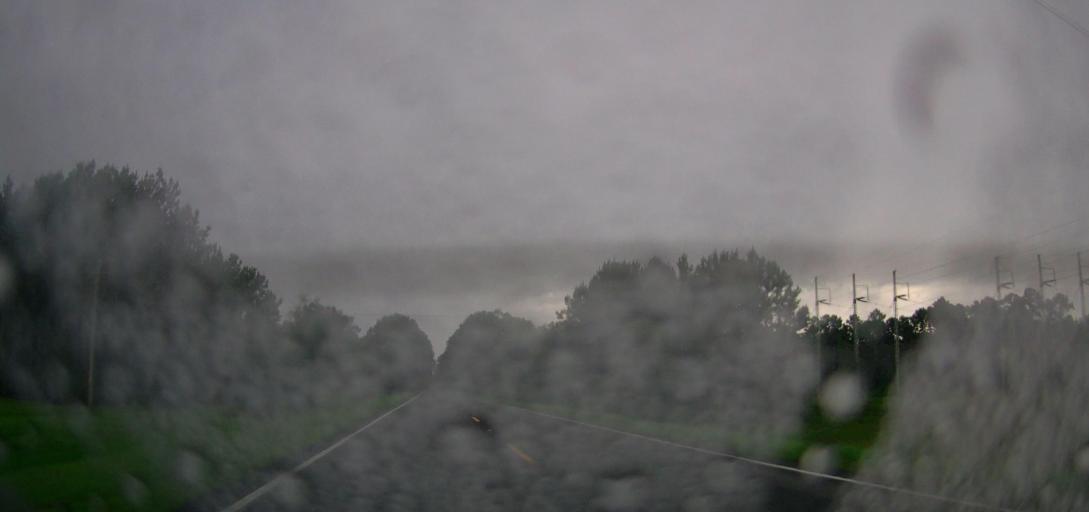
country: US
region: Georgia
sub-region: Glynn County
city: Dock Junction
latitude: 31.2821
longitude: -81.6670
